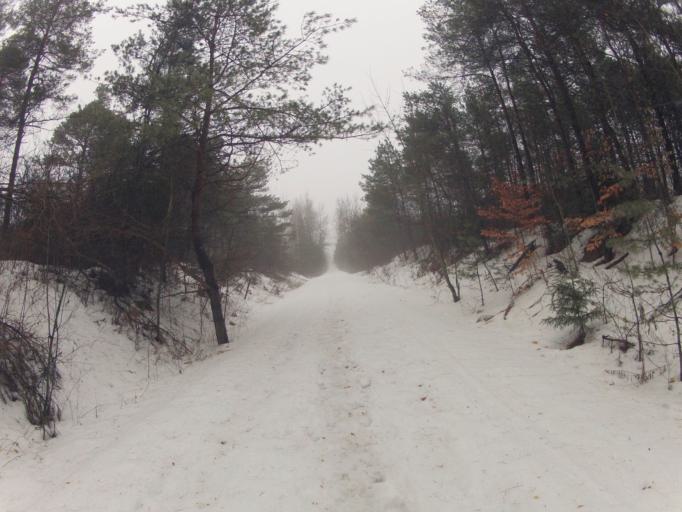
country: CA
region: Ontario
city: Brampton
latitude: 43.8395
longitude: -79.8883
